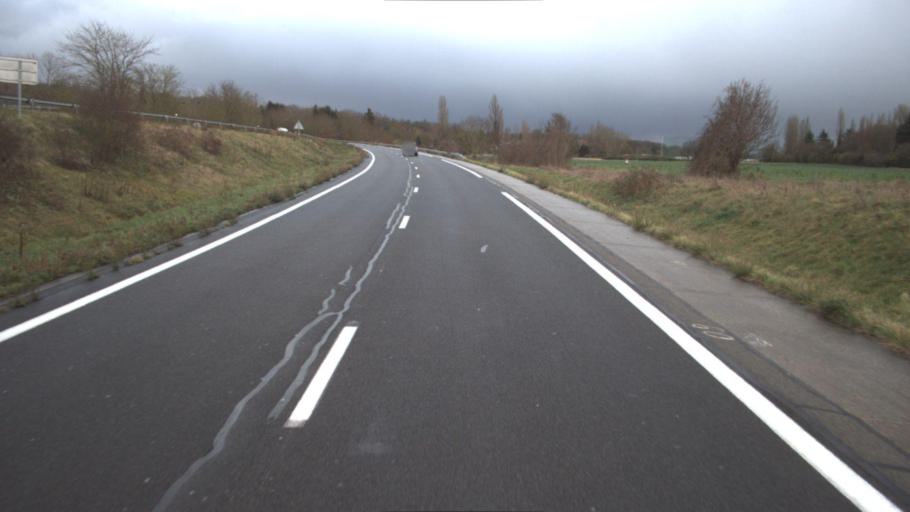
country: FR
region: Ile-de-France
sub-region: Departement de Seine-et-Marne
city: Cely
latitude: 48.4732
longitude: 2.5183
